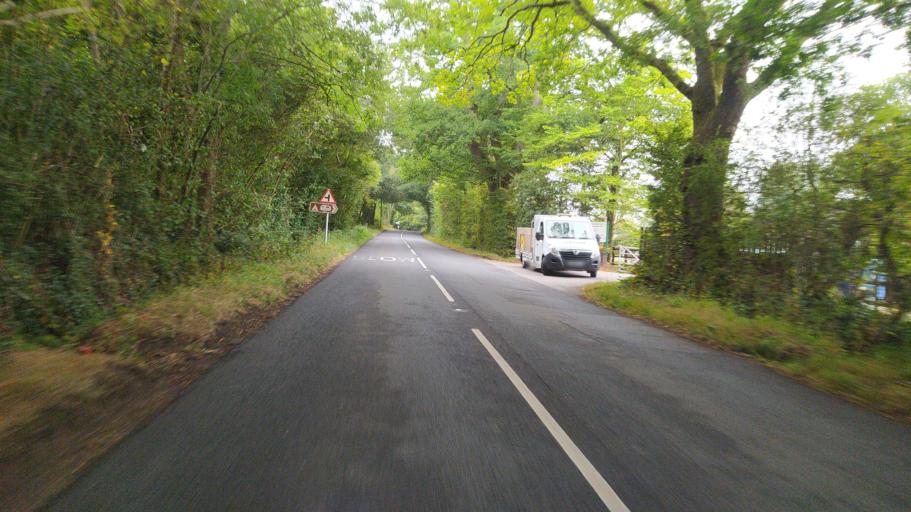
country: GB
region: England
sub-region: Dorset
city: Verwood
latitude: 50.8854
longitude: -1.9050
